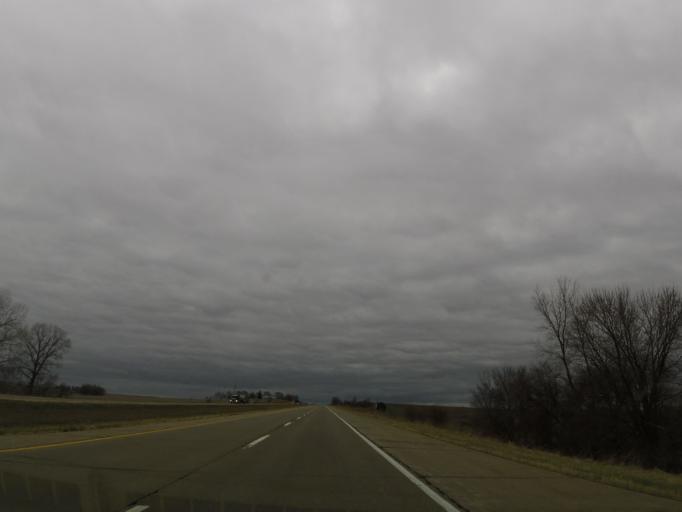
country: US
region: Iowa
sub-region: Benton County
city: Urbana
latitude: 42.2955
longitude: -91.9578
